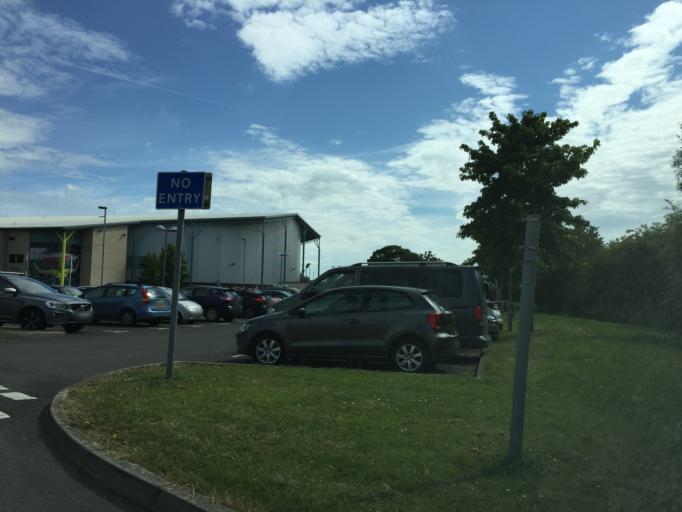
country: GB
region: Wales
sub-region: Newport
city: Nash
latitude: 51.5731
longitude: -2.9587
